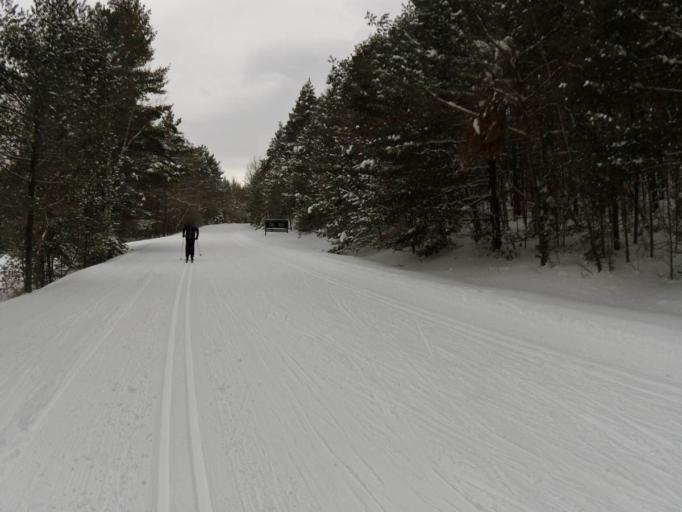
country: CA
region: Quebec
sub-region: Outaouais
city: Wakefield
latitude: 45.6136
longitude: -76.0110
